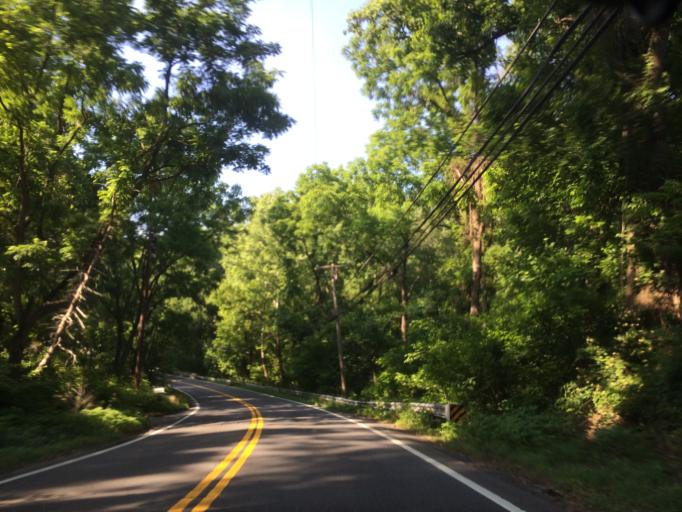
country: US
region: Maryland
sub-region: Montgomery County
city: Olney
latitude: 39.2084
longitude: -77.0629
